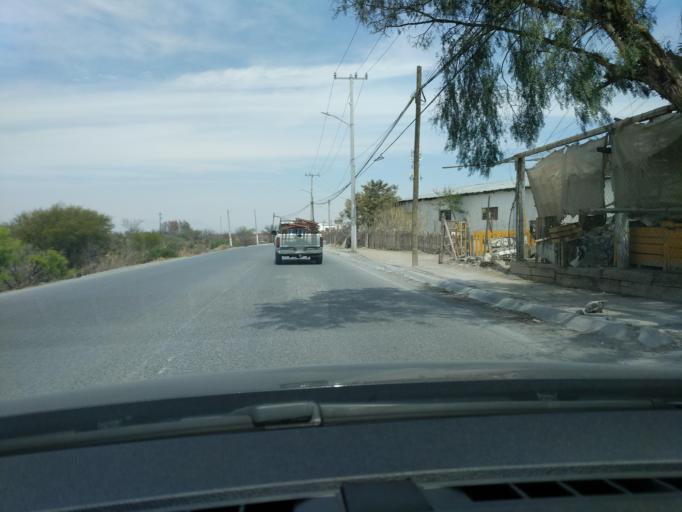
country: MX
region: Coahuila
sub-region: Arteaga
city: Arteaga
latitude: 25.4310
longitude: -100.9130
